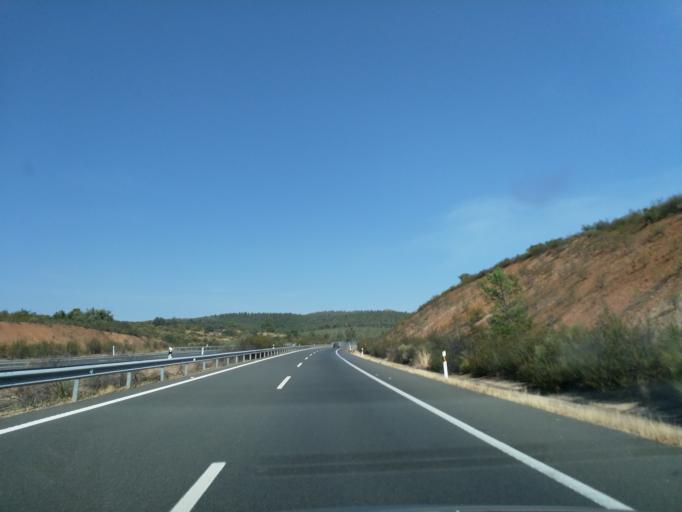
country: ES
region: Extremadura
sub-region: Provincia de Caceres
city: Alcuescar
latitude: 39.1465
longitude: -6.2747
